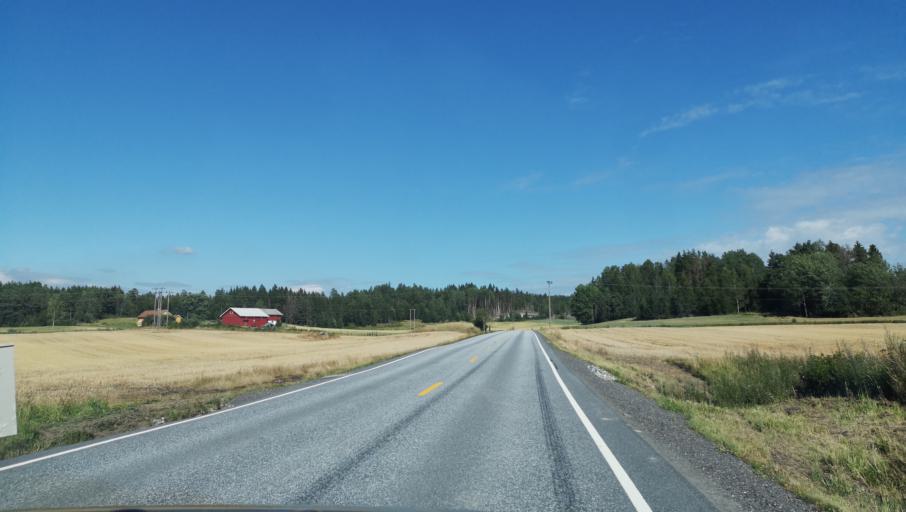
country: NO
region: Akershus
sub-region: Vestby
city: Vestby
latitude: 59.5505
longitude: 10.8088
